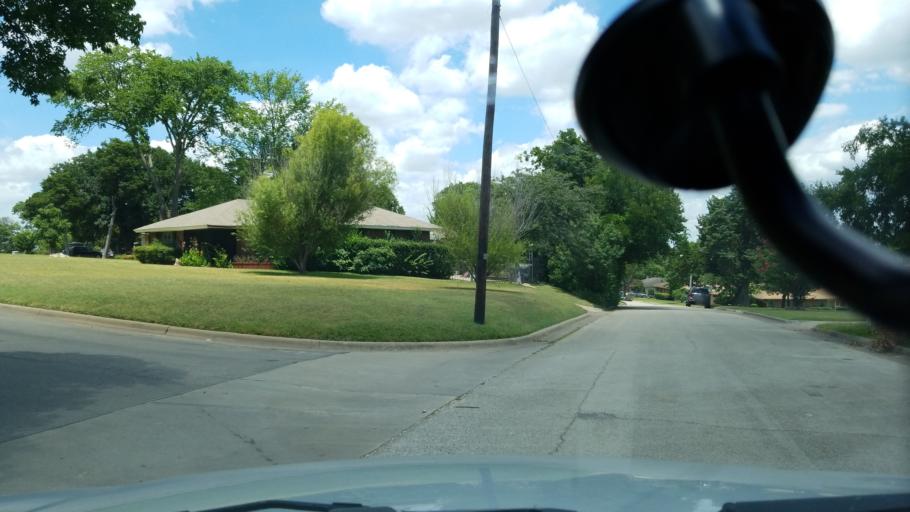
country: US
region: Texas
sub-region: Dallas County
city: Cockrell Hill
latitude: 32.7029
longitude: -96.8778
